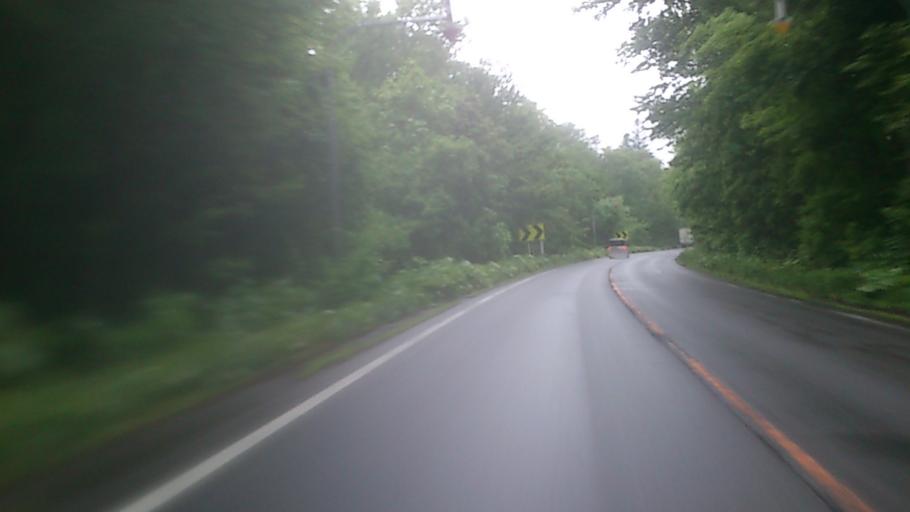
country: JP
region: Hokkaido
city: Chitose
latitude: 42.7905
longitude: 141.4915
